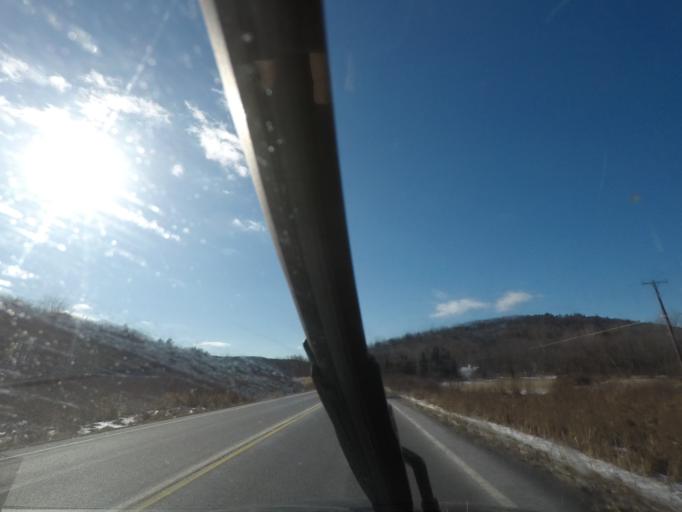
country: US
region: Massachusetts
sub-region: Berkshire County
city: Richmond
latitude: 42.4191
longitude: -73.4708
